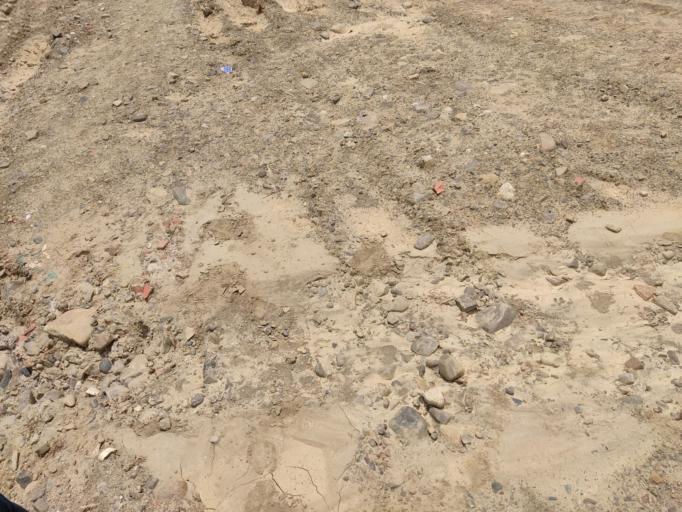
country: BO
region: La Paz
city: La Paz
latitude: -16.5048
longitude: -68.0959
